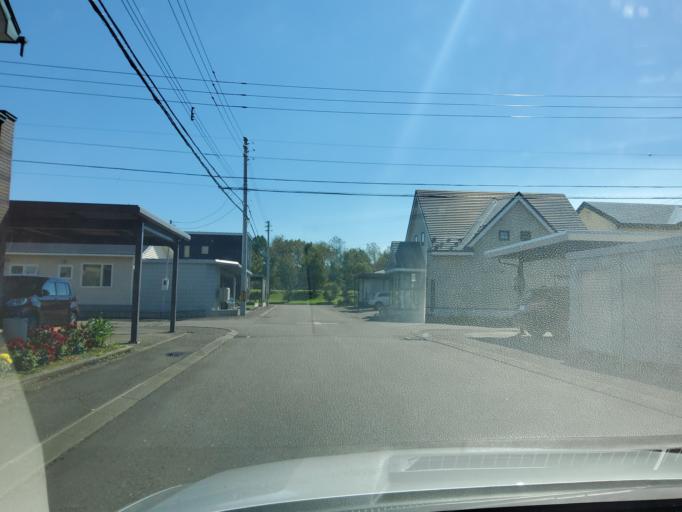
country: JP
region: Hokkaido
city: Obihiro
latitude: 42.9401
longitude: 143.2201
